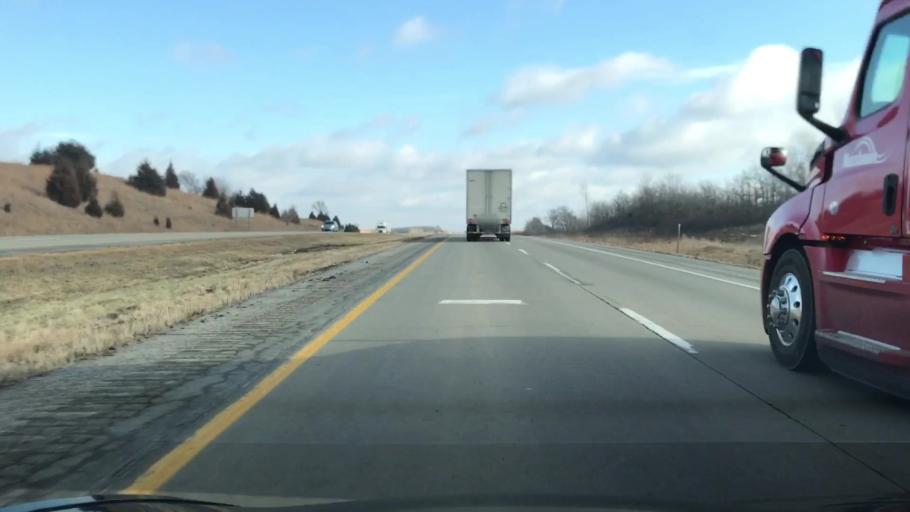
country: US
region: Iowa
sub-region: Cass County
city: Atlantic
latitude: 41.4970
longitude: -94.9175
